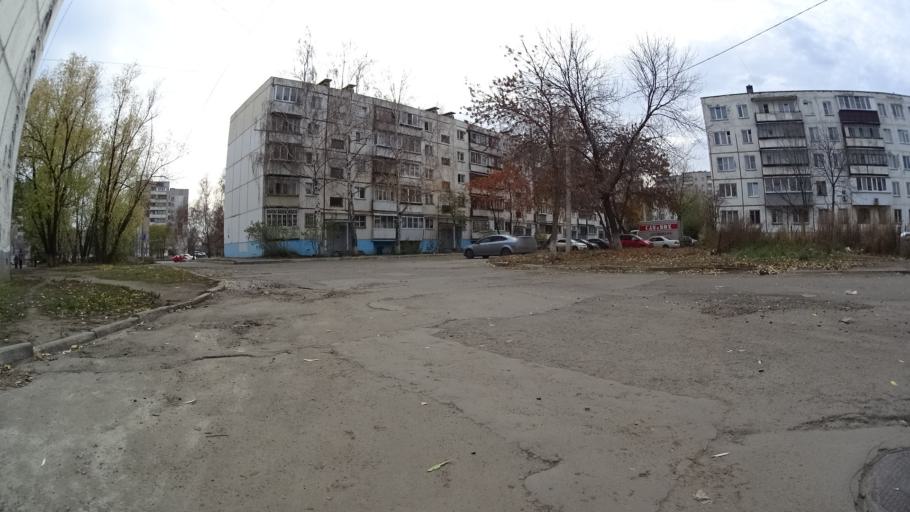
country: RU
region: Chelyabinsk
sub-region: Gorod Chelyabinsk
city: Chelyabinsk
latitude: 55.1898
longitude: 61.3161
